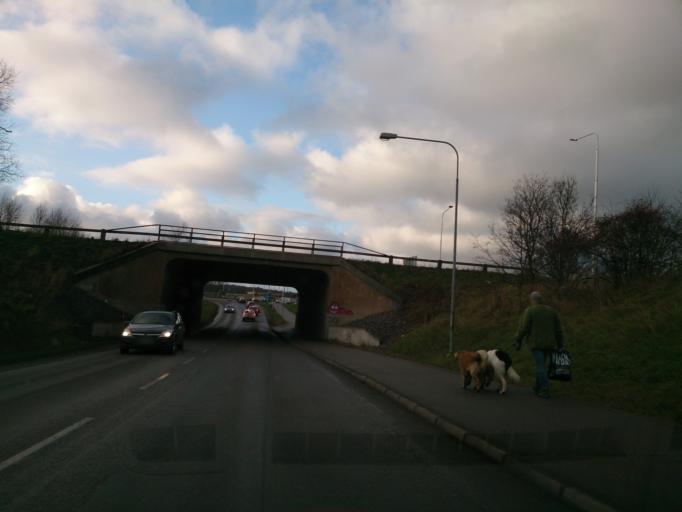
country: SE
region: OEstergoetland
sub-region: Norrkopings Kommun
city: Norrkoping
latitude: 58.6175
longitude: 16.1605
